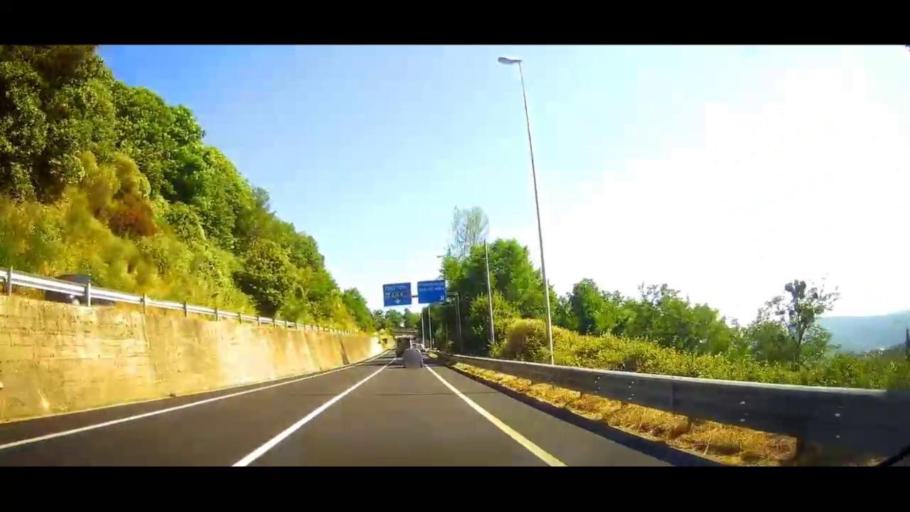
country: IT
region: Calabria
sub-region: Provincia di Cosenza
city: Spezzano della Sila
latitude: 39.2990
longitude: 16.3423
